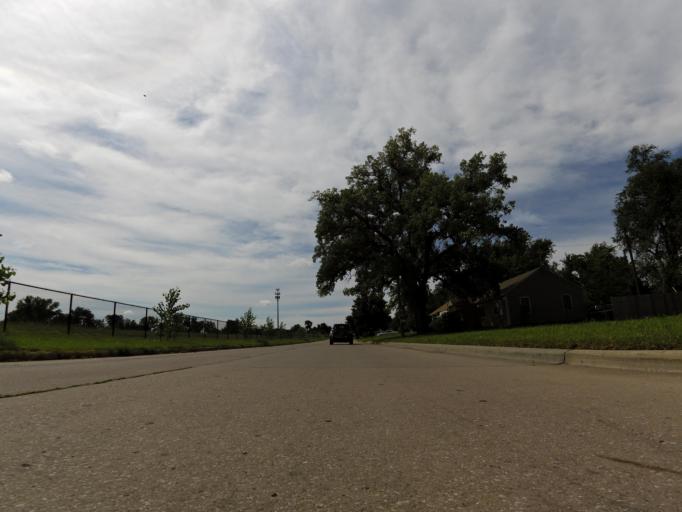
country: US
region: Kansas
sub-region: Sedgwick County
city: Wichita
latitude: 37.7056
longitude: -97.2918
